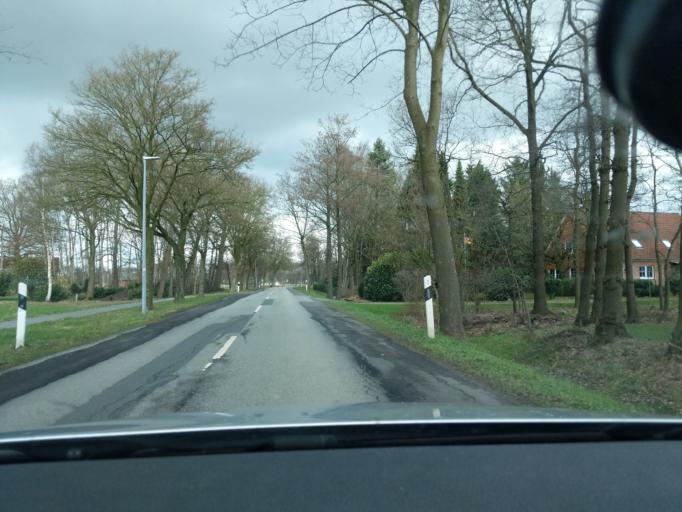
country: DE
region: Lower Saxony
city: Stade
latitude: 53.6511
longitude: 9.4323
